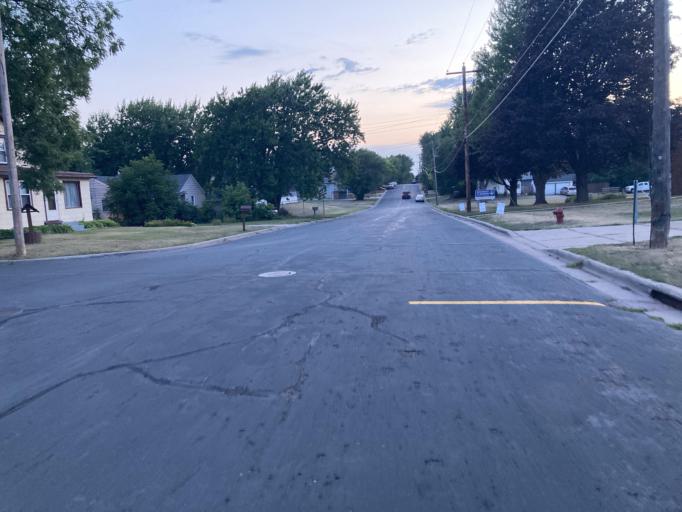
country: US
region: Minnesota
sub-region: Dakota County
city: West Saint Paul
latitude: 44.9178
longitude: -93.0703
